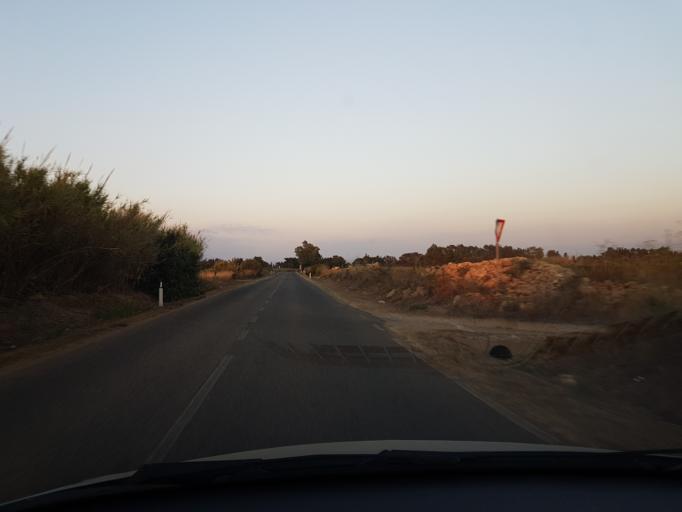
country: IT
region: Sardinia
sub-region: Provincia di Oristano
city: Riola Sardo
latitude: 39.9977
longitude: 8.4857
